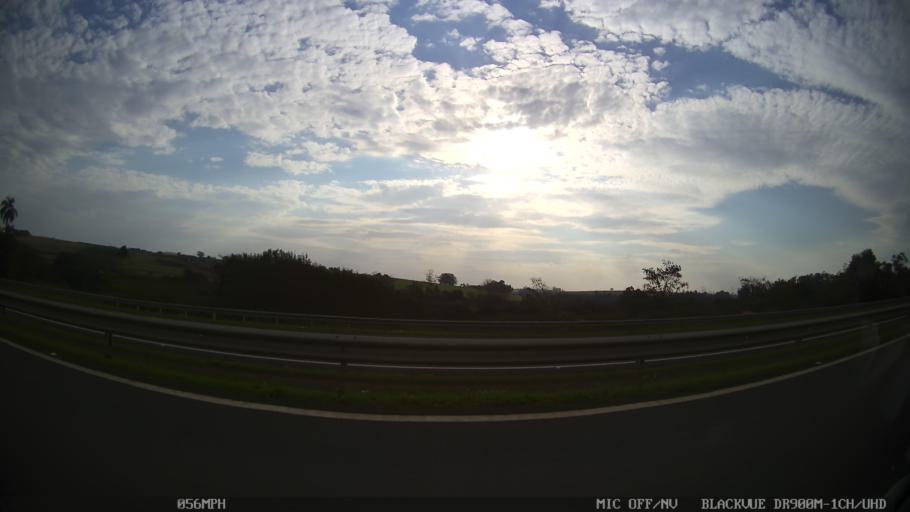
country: BR
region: Sao Paulo
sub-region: Cosmopolis
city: Cosmopolis
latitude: -22.6133
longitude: -47.1958
